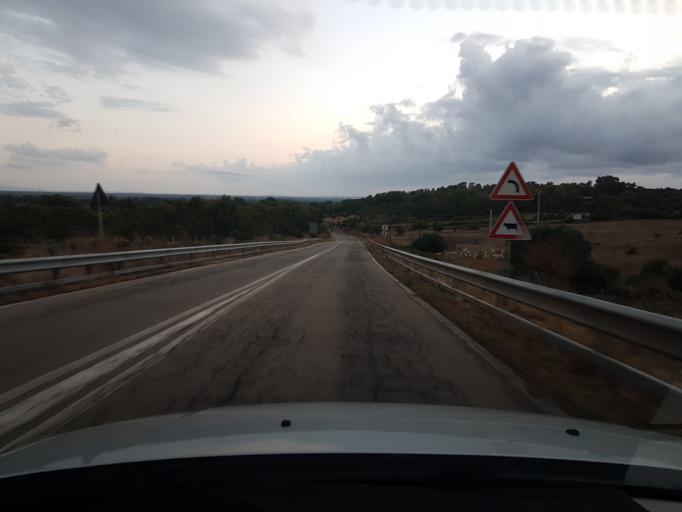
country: IT
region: Sardinia
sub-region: Provincia di Oristano
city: Milis
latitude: 40.0533
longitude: 8.6333
